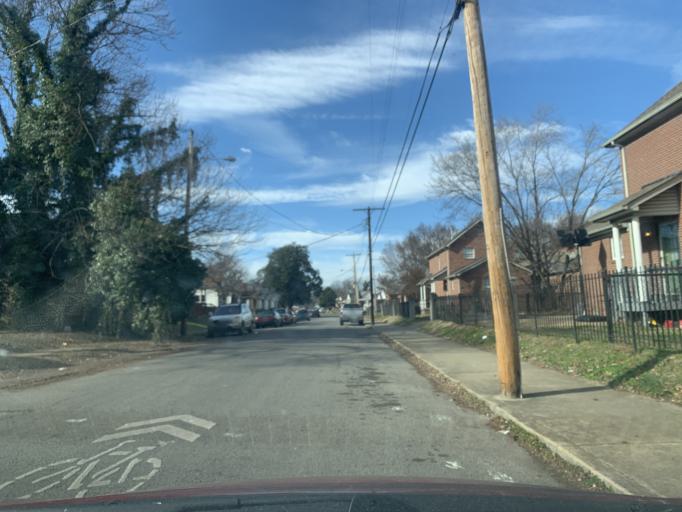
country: US
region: Kentucky
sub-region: Jefferson County
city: Louisville
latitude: 38.2324
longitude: -85.7947
